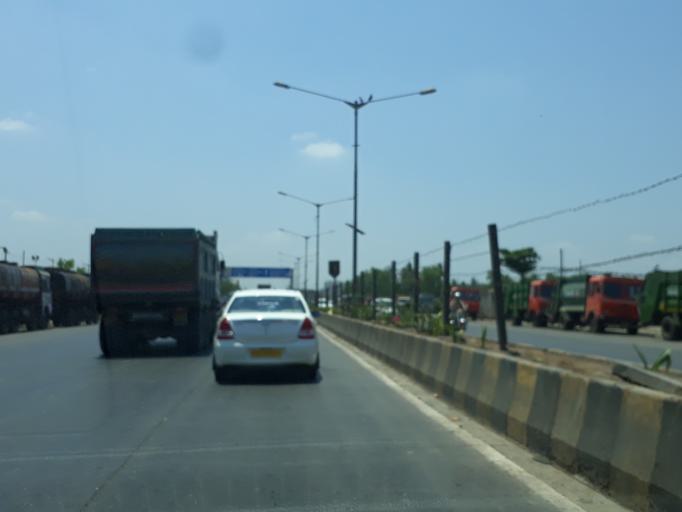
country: IN
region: Maharashtra
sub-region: Mumbai Suburban
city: Mumbai
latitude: 19.0605
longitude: 72.9212
